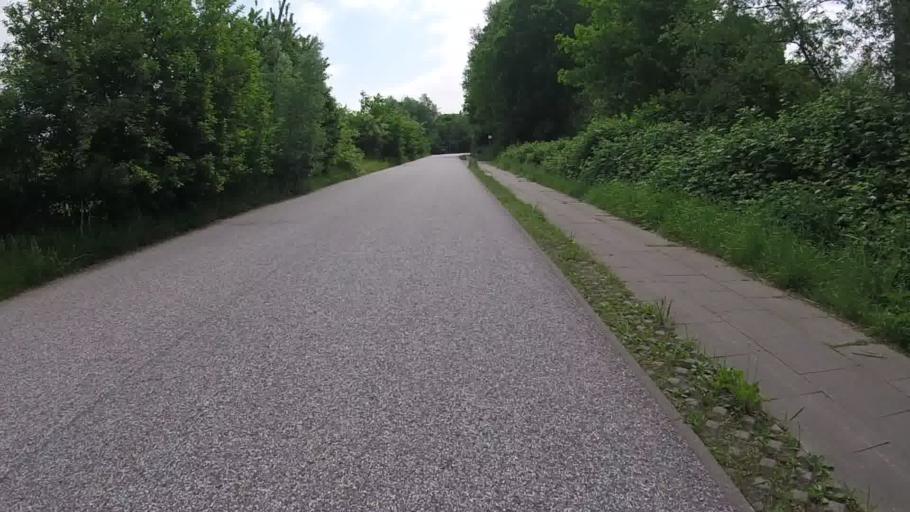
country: DE
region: Hamburg
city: Wandsbek
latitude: 53.5139
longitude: 10.1029
